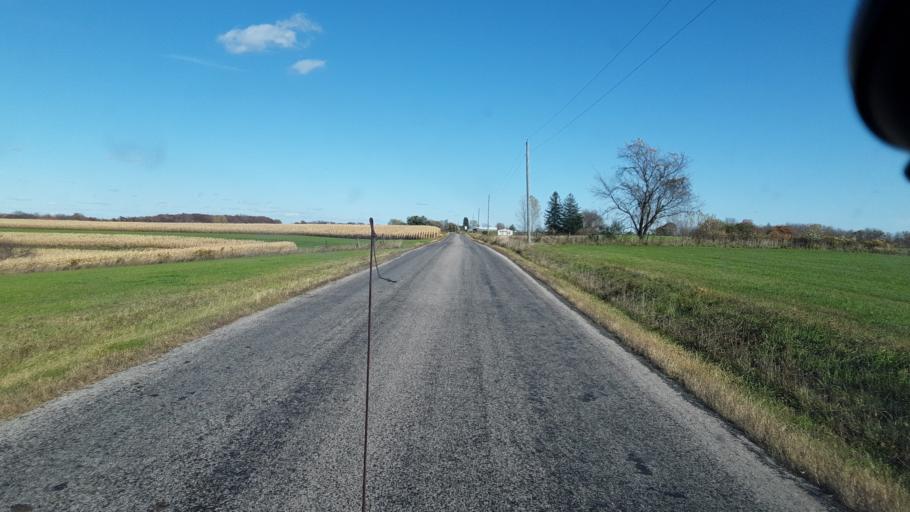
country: US
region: Wisconsin
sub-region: Vernon County
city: Hillsboro
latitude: 43.6853
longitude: -90.4184
